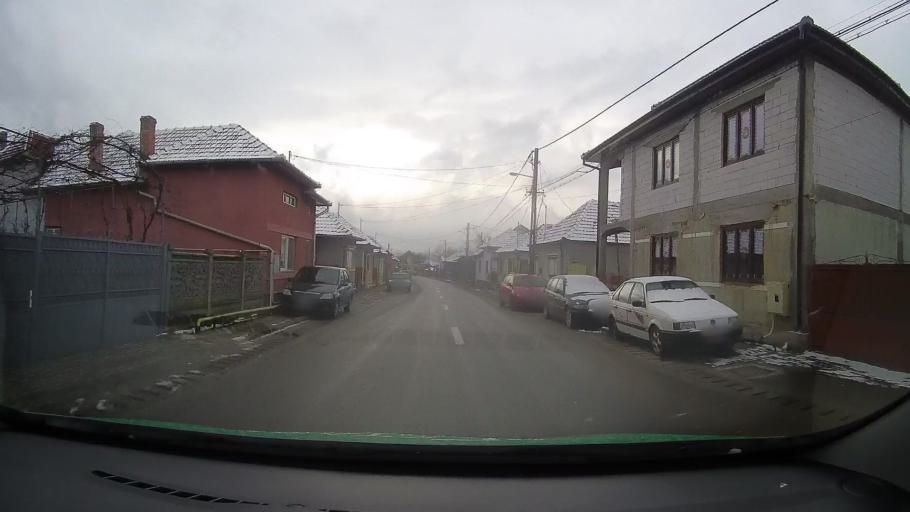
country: RO
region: Hunedoara
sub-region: Oras Hateg
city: Hateg
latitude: 45.6146
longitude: 22.9447
